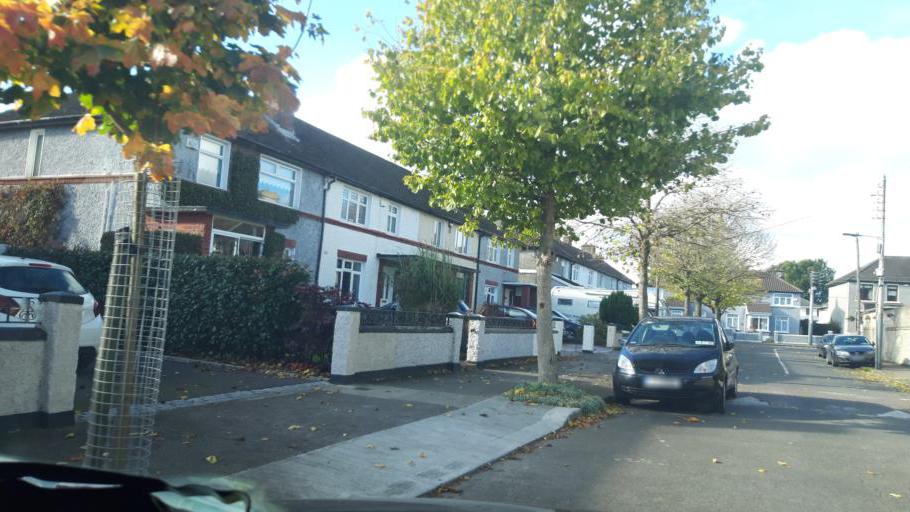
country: IE
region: Leinster
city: Marino
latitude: 53.3744
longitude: -6.2254
